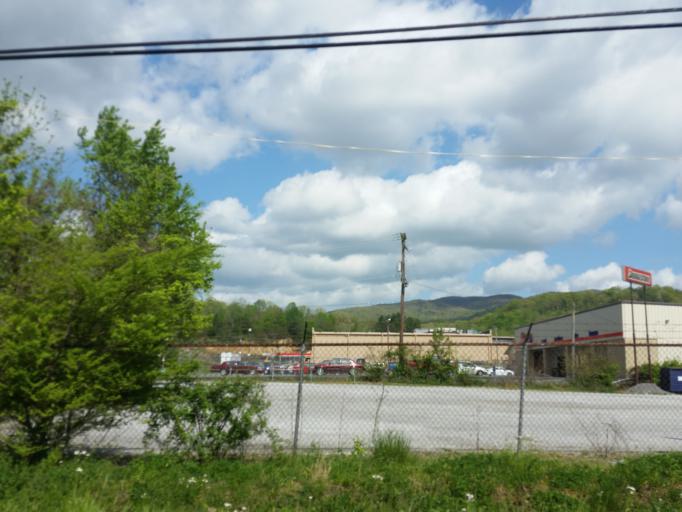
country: US
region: Kentucky
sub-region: Bell County
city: Middlesboro
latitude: 36.6139
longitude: -83.7072
